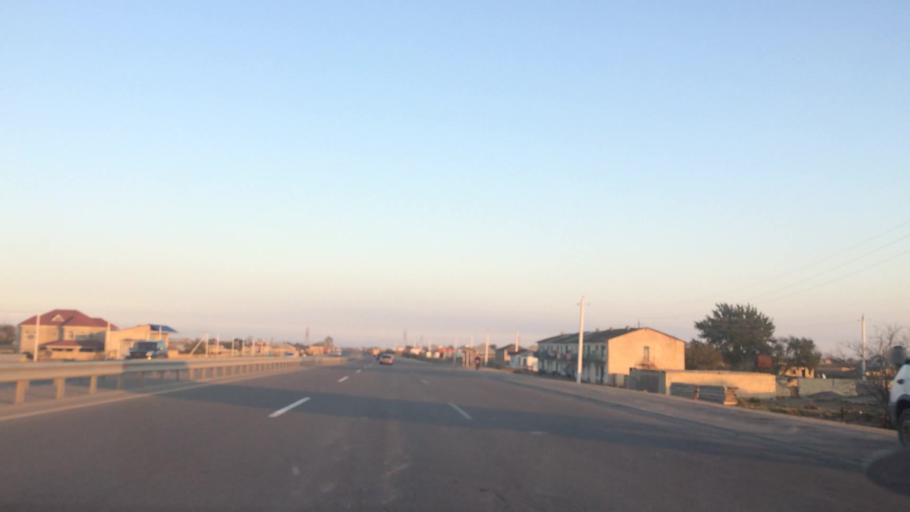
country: AZ
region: Baki
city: Qobustan
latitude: 39.9725
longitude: 49.2561
